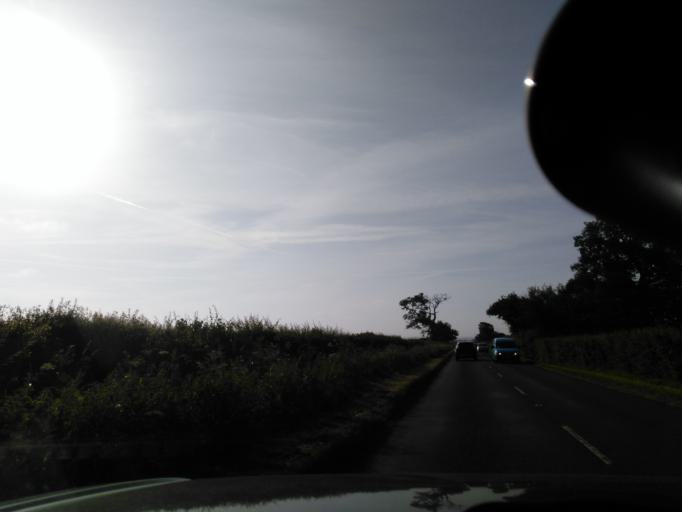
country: GB
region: England
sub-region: Wiltshire
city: Bulkington
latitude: 51.3295
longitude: -2.0703
